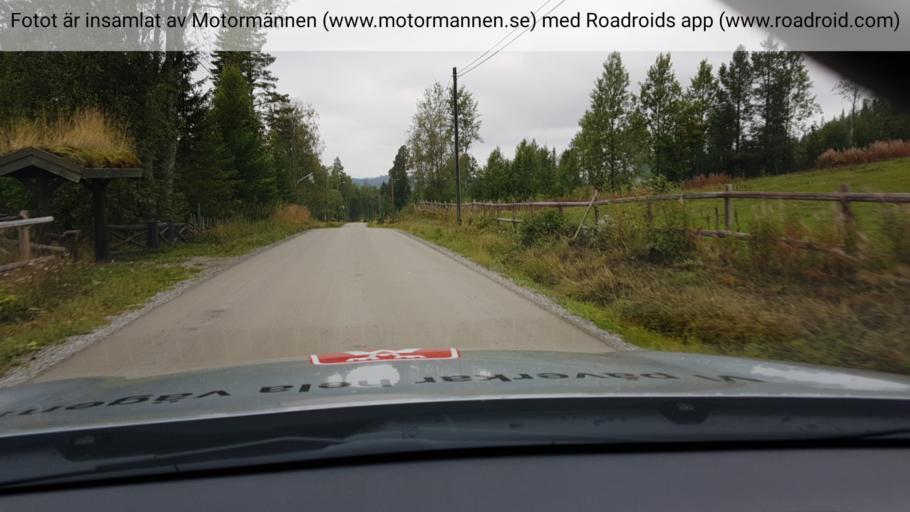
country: SE
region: Jaemtland
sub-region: Braecke Kommun
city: Braecke
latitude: 62.7718
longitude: 15.4831
